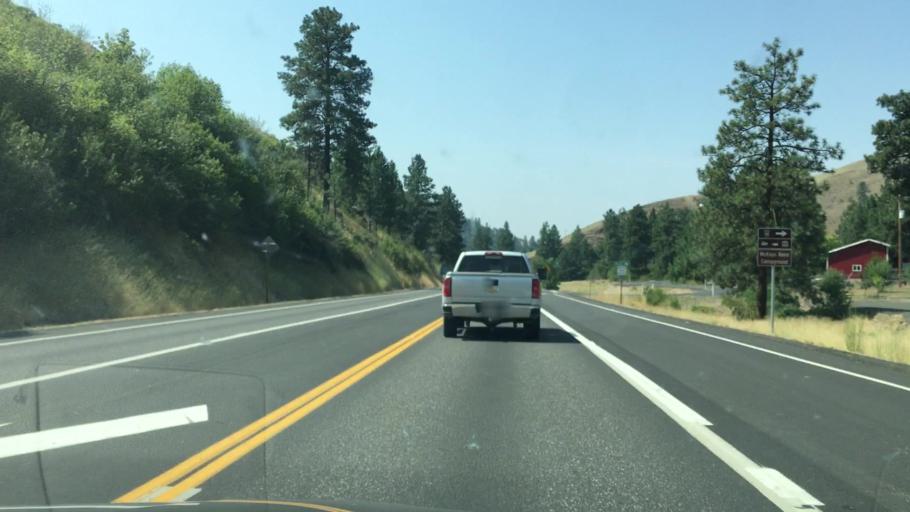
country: US
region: Idaho
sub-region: Nez Perce County
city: Lapwai
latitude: 46.4995
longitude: -116.7226
